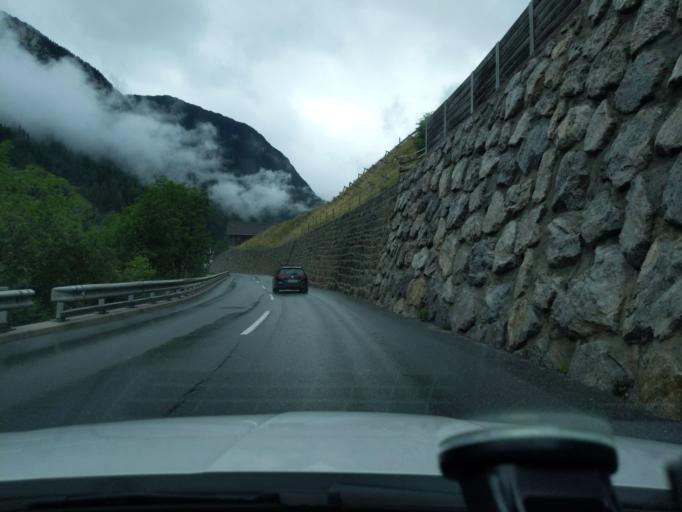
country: AT
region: Tyrol
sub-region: Politischer Bezirk Schwaz
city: Mayrhofen
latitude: 47.1501
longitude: 11.7989
